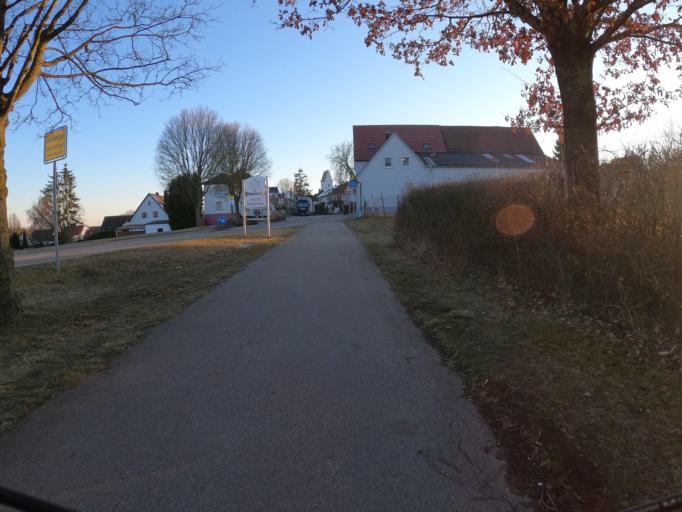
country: DE
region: Baden-Wuerttemberg
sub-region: Tuebingen Region
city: Langenau
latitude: 48.4634
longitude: 10.1046
